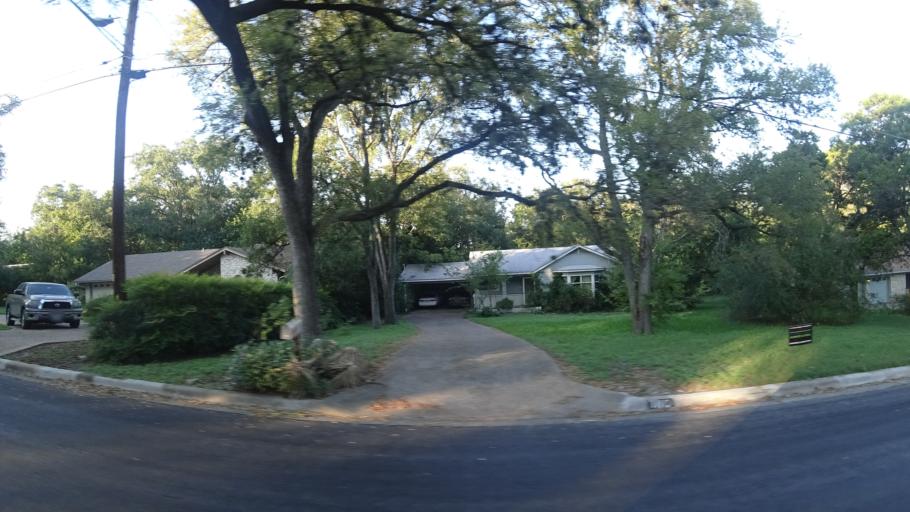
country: US
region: Texas
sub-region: Travis County
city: Wells Branch
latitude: 30.3655
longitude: -97.6734
